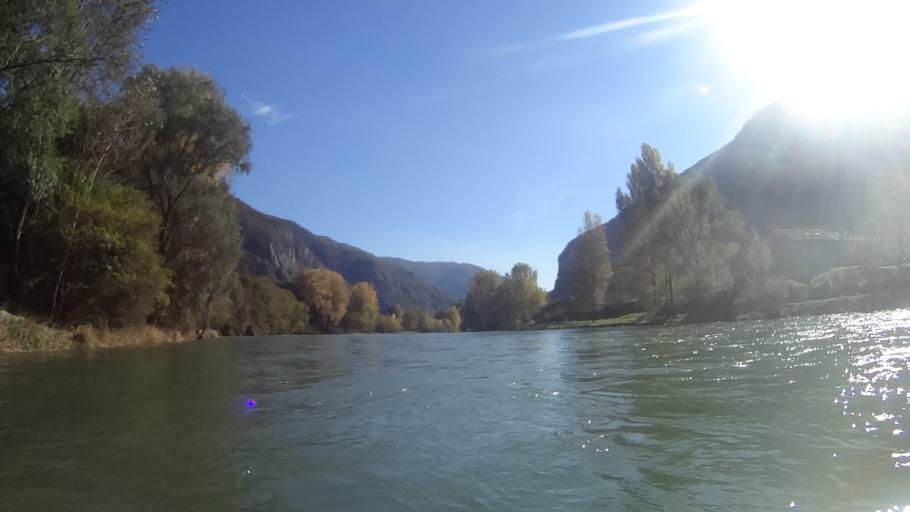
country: IT
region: Veneto
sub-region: Provincia di Vicenza
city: San Nazario
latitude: 45.8413
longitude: 11.6829
